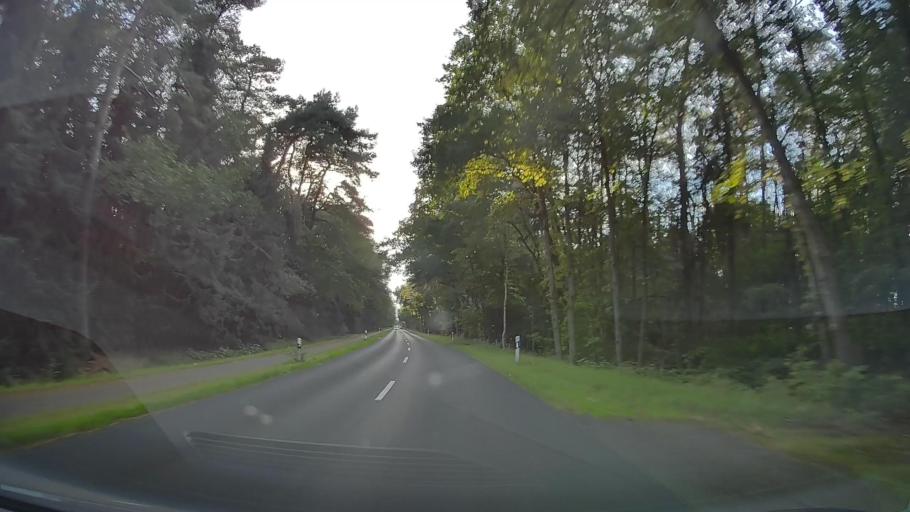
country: DE
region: Lower Saxony
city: Hellwege
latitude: 53.0740
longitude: 9.2047
